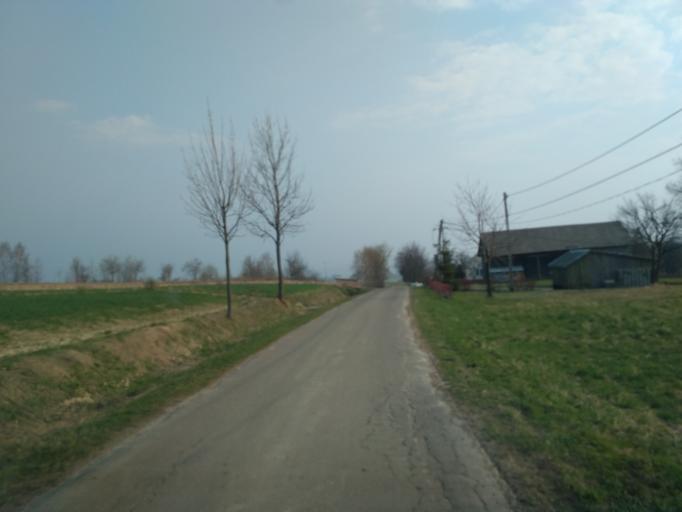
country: PL
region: Subcarpathian Voivodeship
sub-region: Powiat ropczycko-sedziszowski
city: Wielopole Skrzynskie
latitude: 49.9096
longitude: 21.5991
